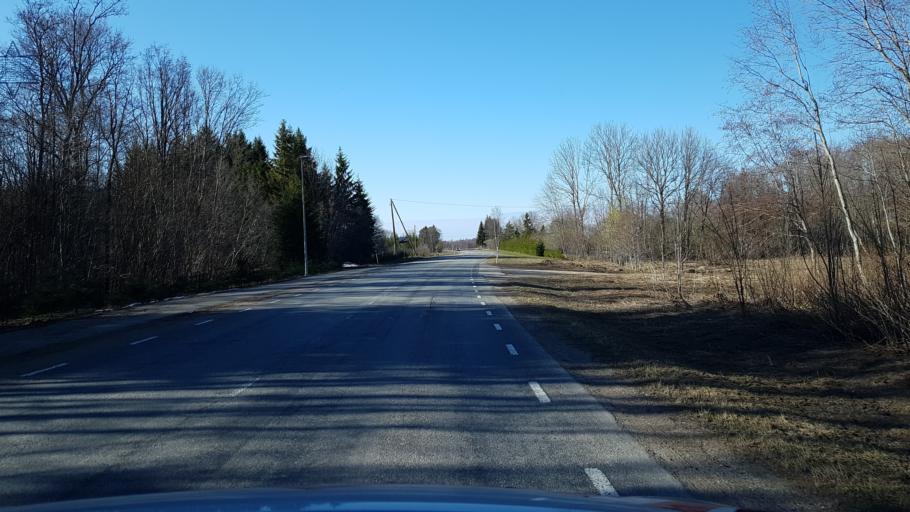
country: EE
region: Laeaene-Virumaa
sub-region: Haljala vald
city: Haljala
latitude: 59.4441
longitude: 26.2535
